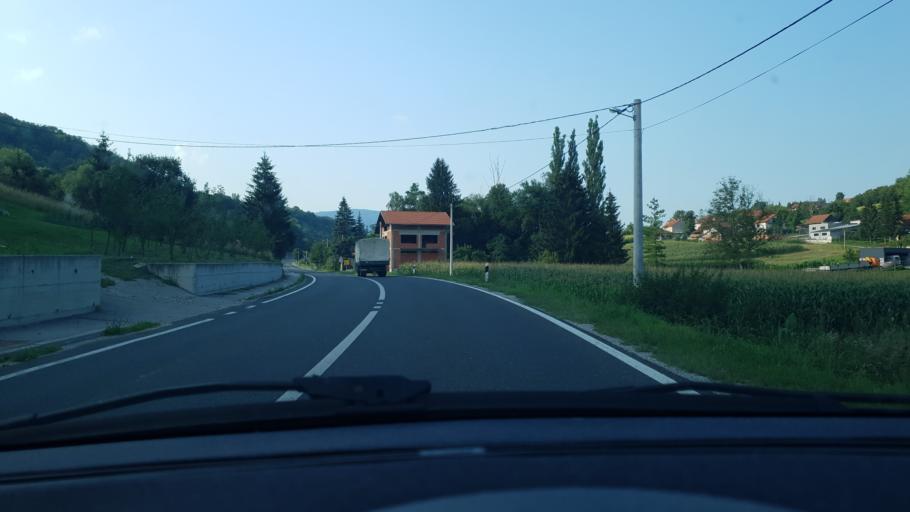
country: HR
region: Krapinsko-Zagorska
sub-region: Grad Krapina
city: Krapina
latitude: 46.1082
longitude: 15.9064
